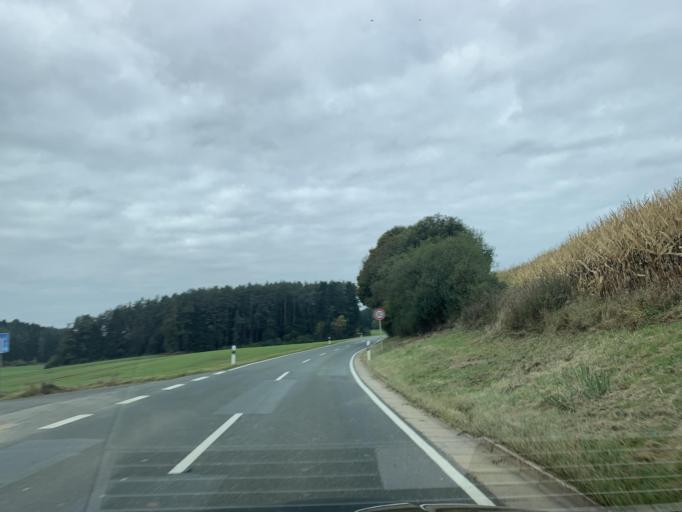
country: DE
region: Bavaria
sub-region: Upper Franconia
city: Pottenstein
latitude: 49.7283
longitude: 11.4526
